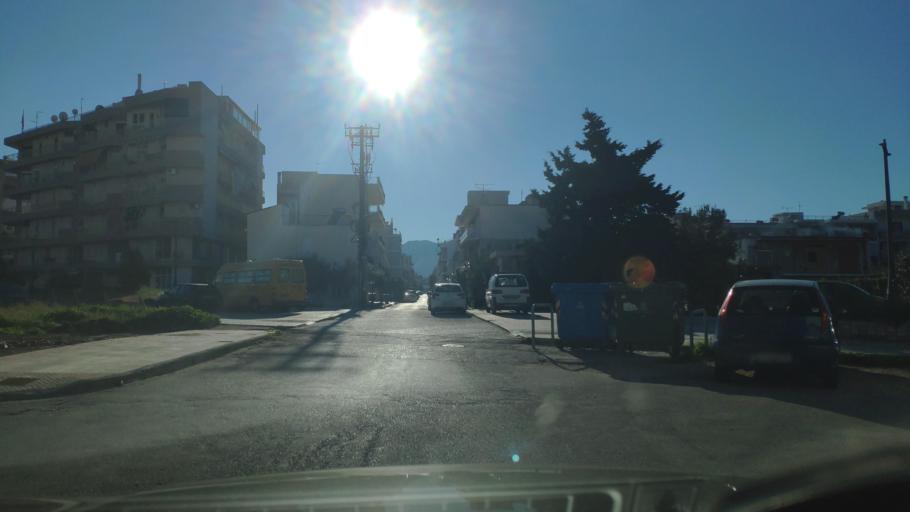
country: GR
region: Peloponnese
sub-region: Nomos Korinthias
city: Korinthos
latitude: 37.9397
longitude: 22.9270
